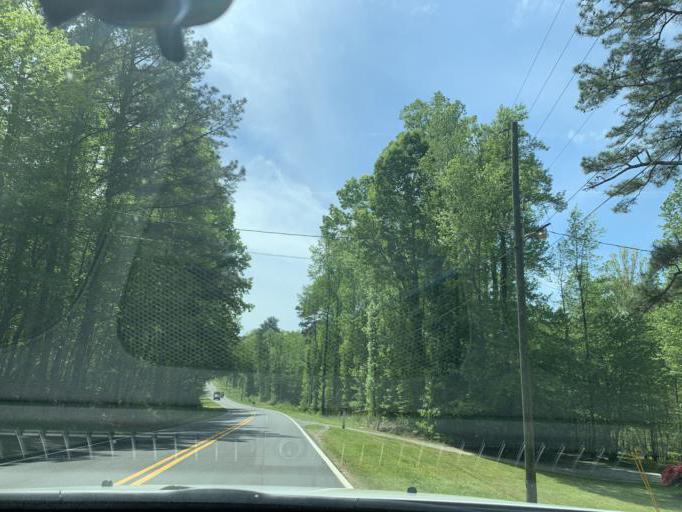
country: US
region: Georgia
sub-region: Forsyth County
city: Cumming
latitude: 34.2527
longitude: -84.1473
